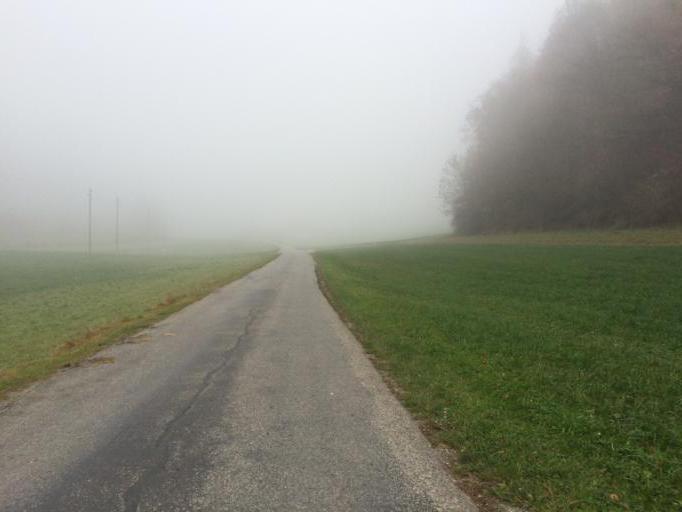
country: CH
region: Bern
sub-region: Bern-Mittelland District
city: Kehrsatz
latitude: 46.9092
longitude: 7.4440
